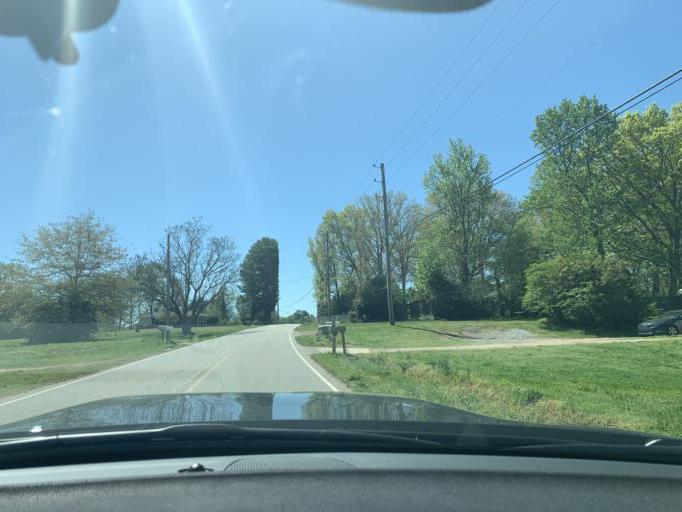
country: US
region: Georgia
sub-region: Forsyth County
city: Cumming
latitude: 34.1795
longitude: -84.1692
